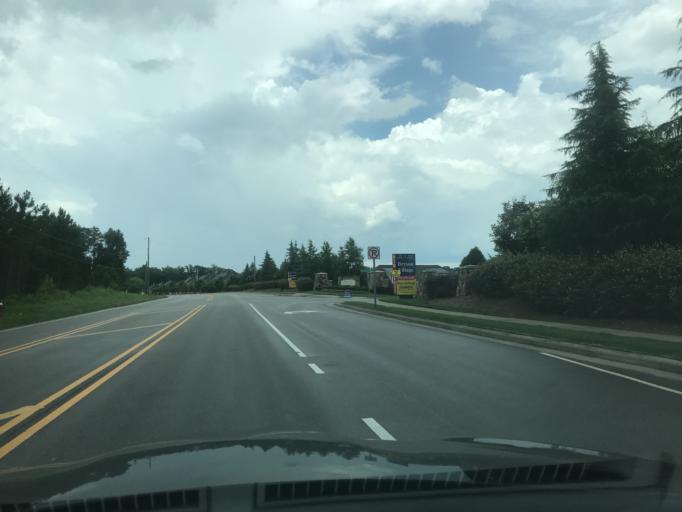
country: US
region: North Carolina
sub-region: Wake County
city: Knightdale
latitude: 35.8416
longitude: -78.5078
